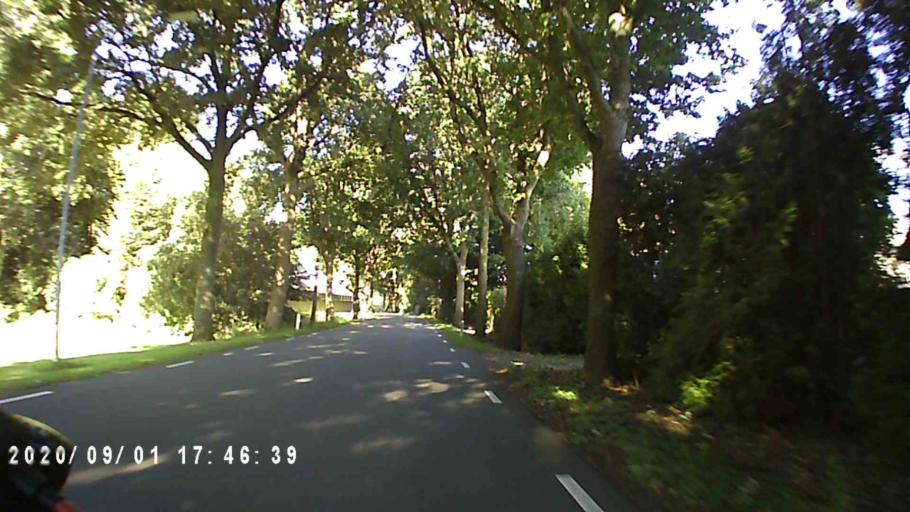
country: NL
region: Groningen
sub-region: Gemeente Hoogezand-Sappemeer
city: Hoogezand
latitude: 53.2166
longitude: 6.7360
